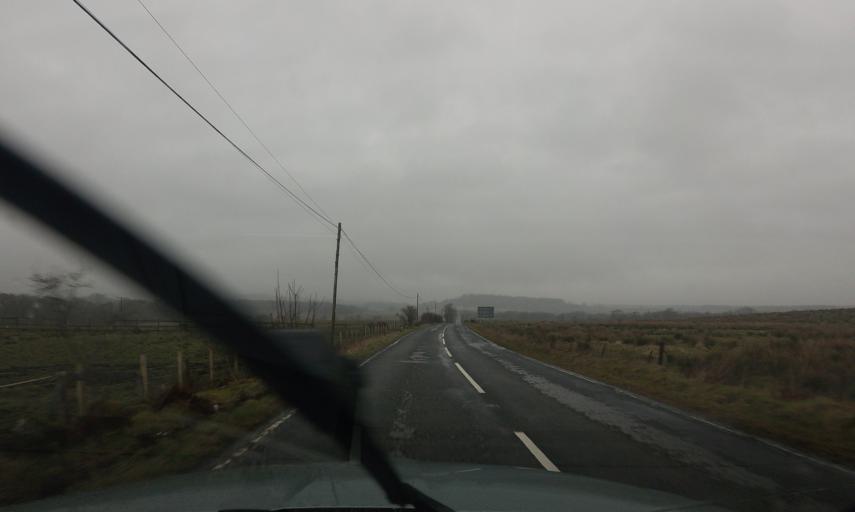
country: GB
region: Scotland
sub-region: Stirling
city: Balfron
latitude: 56.1211
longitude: -4.3595
